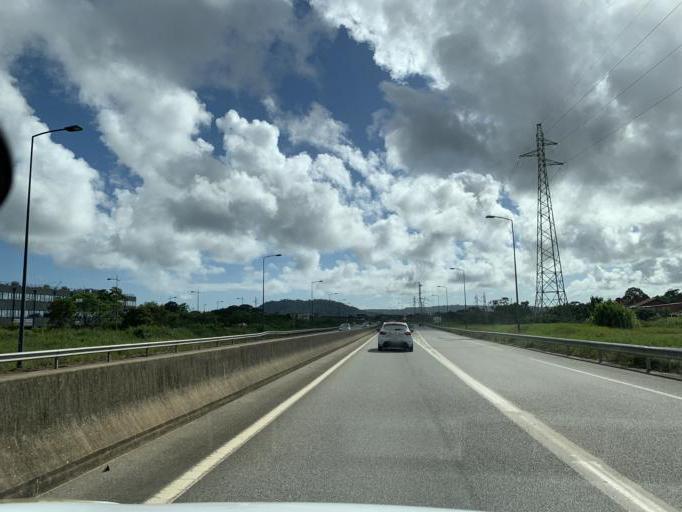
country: GF
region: Guyane
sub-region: Guyane
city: Cayenne
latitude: 4.8912
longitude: -52.3383
